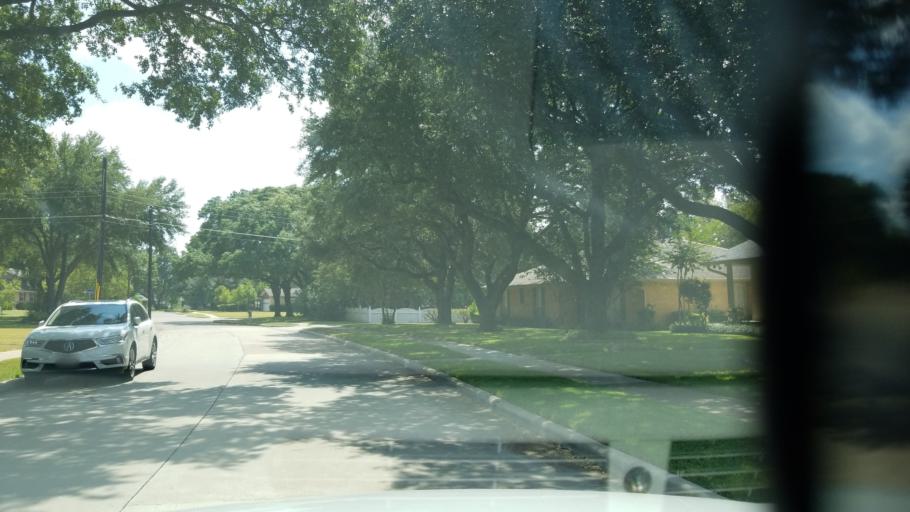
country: US
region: Texas
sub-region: Dallas County
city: Richardson
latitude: 32.9653
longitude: -96.7671
